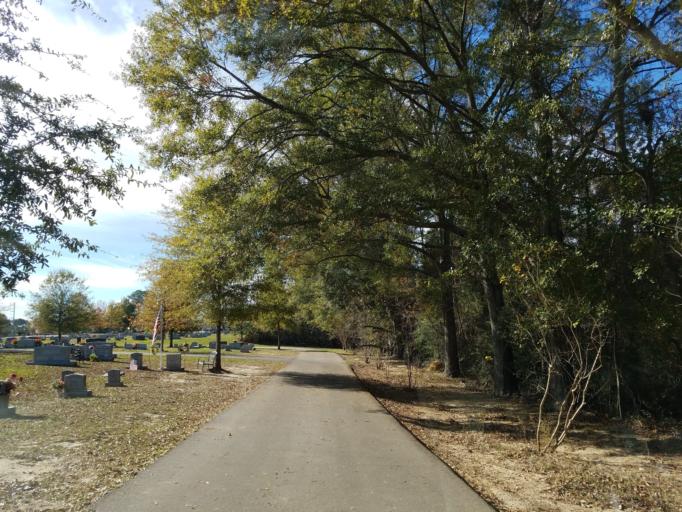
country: US
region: Mississippi
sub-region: Lamar County
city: Arnold Line
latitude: 31.3383
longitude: -89.3372
